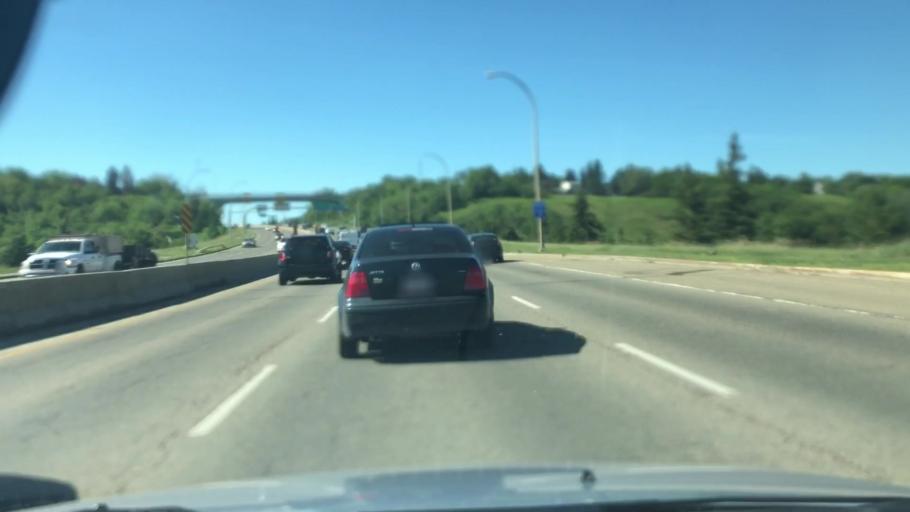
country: CA
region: Alberta
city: Edmonton
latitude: 53.5576
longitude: -113.4397
